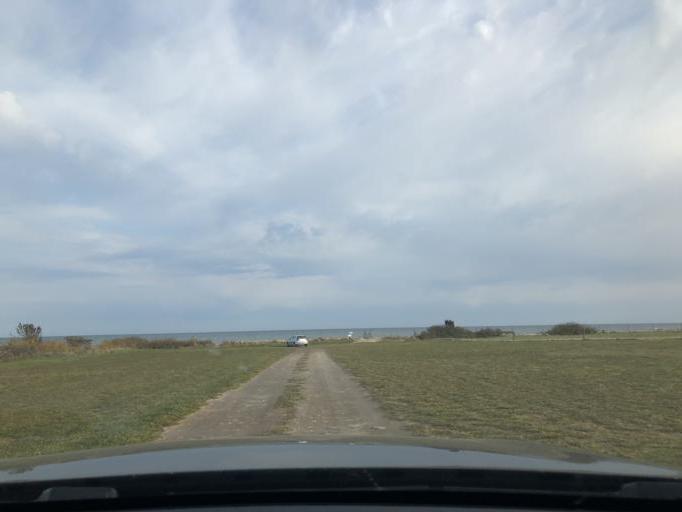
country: SE
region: Kalmar
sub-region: Morbylanga Kommun
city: Sodra Sandby
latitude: 56.5542
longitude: 16.6406
